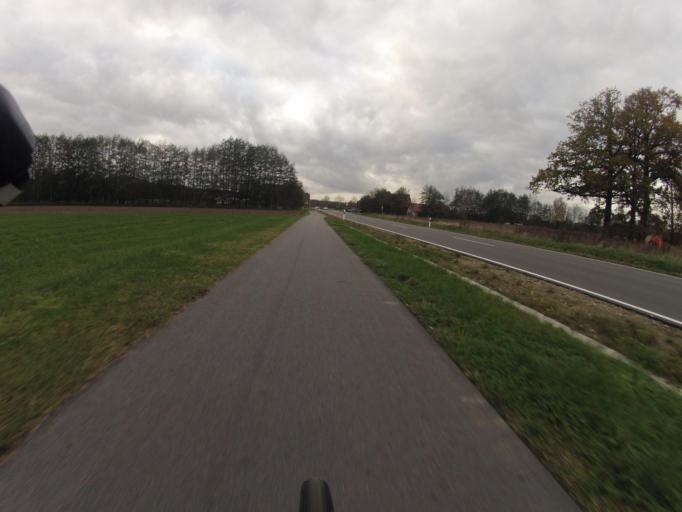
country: DE
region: North Rhine-Westphalia
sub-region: Regierungsbezirk Munster
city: Birgte
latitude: 52.2786
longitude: 7.6531
